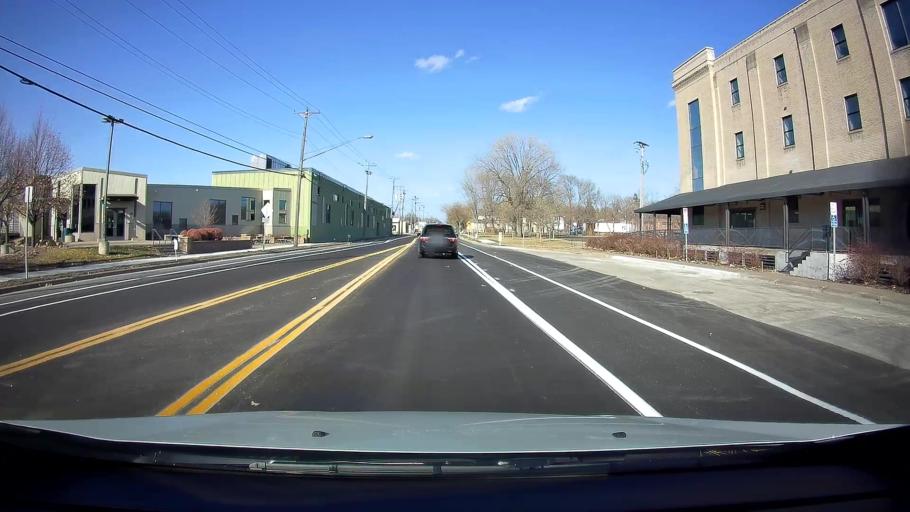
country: US
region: Minnesota
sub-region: Ramsey County
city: Falcon Heights
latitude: 44.9573
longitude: -93.1772
